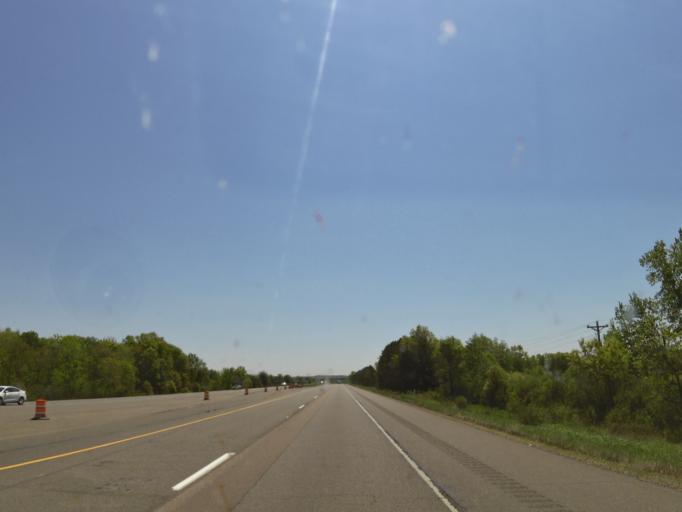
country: US
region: Wisconsin
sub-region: Monroe County
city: Tomah
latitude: 44.0090
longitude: -90.4856
